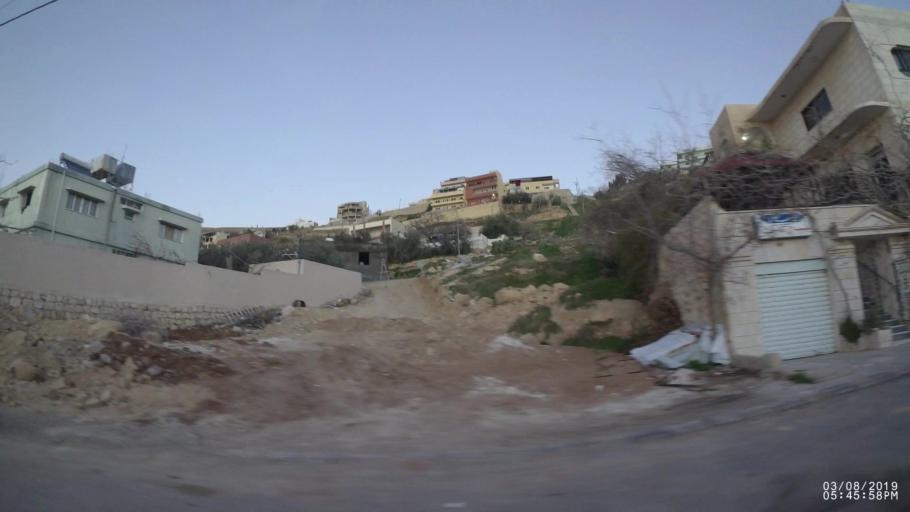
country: JO
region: Ma'an
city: Petra
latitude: 30.3167
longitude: 35.4823
